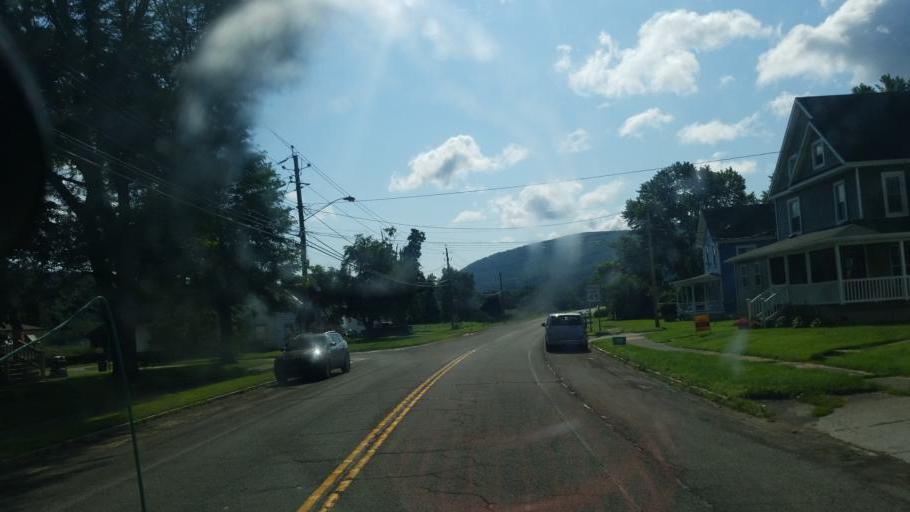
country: US
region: New York
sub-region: Steuben County
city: Canisteo
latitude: 42.2682
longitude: -77.5988
